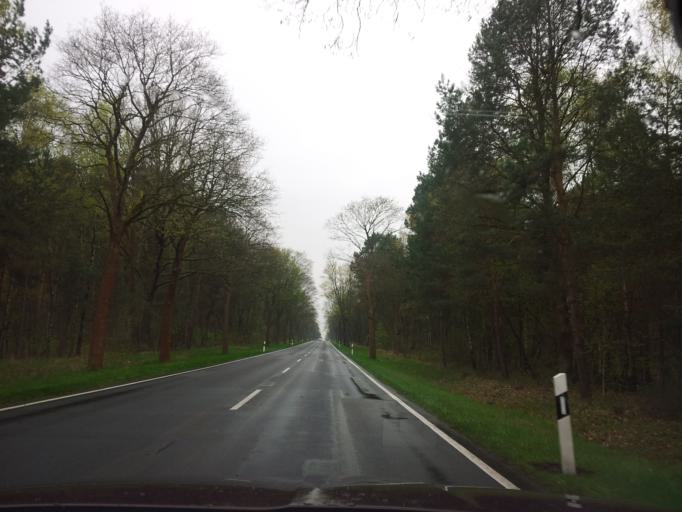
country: DE
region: Brandenburg
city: Treuenbrietzen
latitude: 52.0568
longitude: 12.8219
